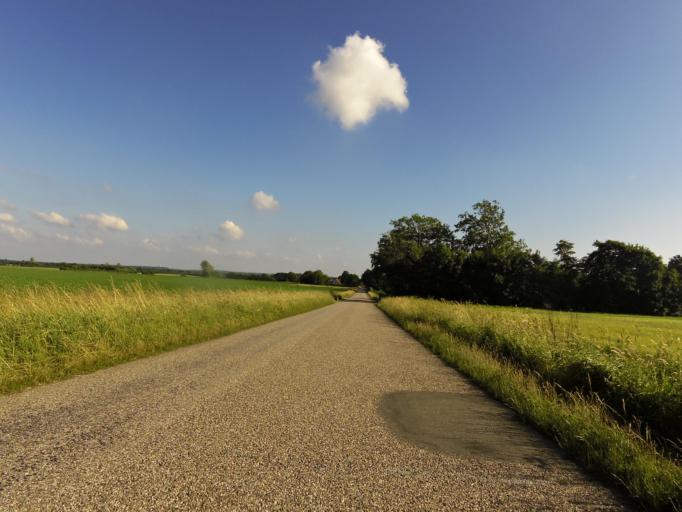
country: DK
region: South Denmark
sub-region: Vejen Kommune
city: Rodding
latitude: 55.3214
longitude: 9.1811
